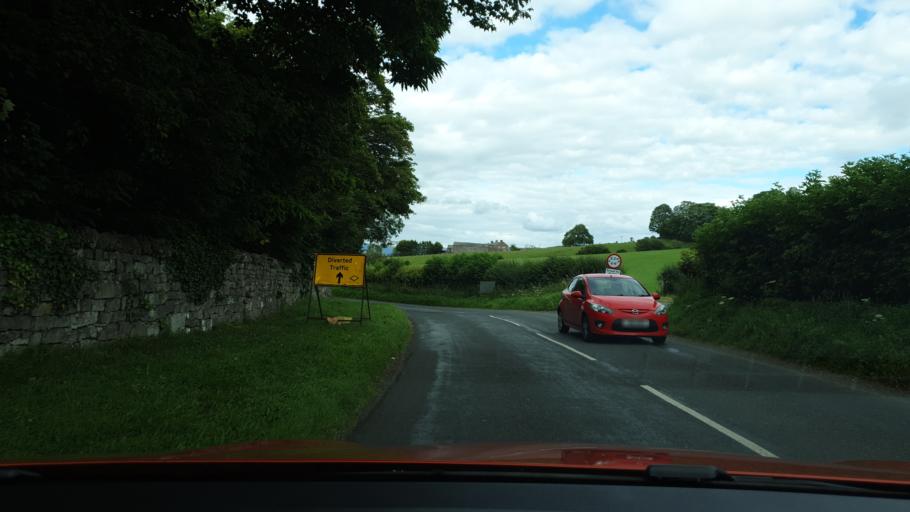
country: GB
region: England
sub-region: Cumbria
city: Penrith
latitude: 54.6194
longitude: -2.8024
